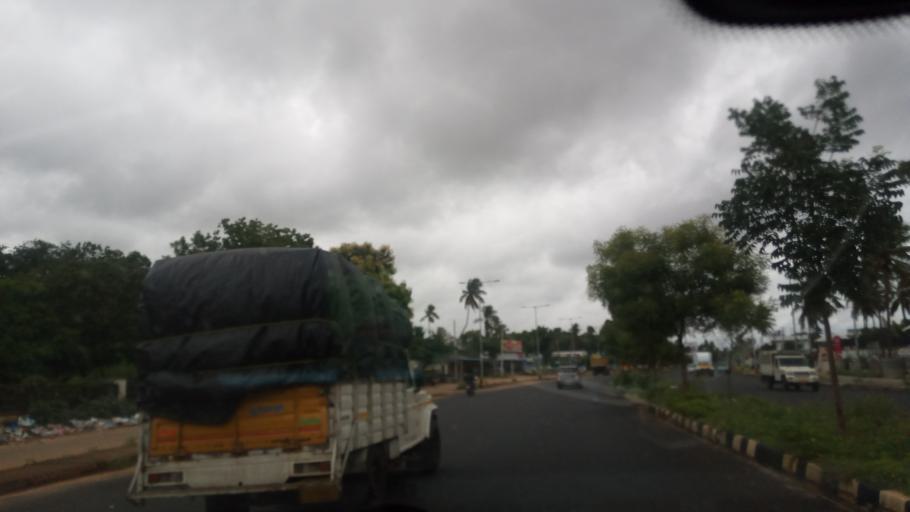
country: IN
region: Karnataka
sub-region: Mysore
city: Mysore
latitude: 12.3005
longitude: 76.6026
